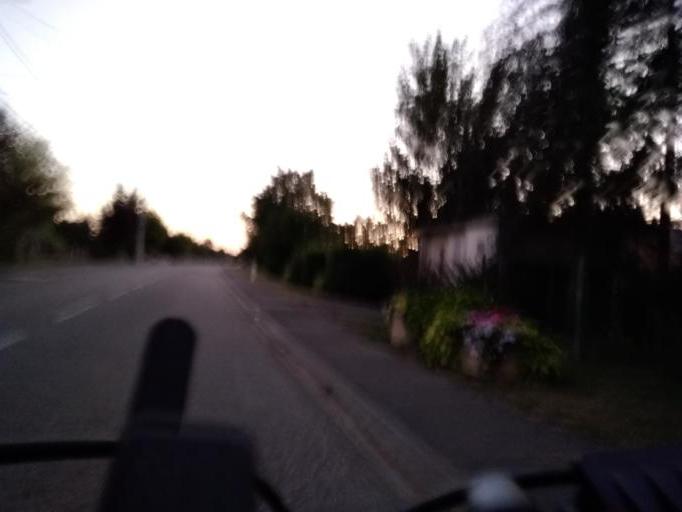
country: FR
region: Lorraine
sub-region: Departement de la Moselle
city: Neufgrange
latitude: 49.0778
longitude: 7.0501
